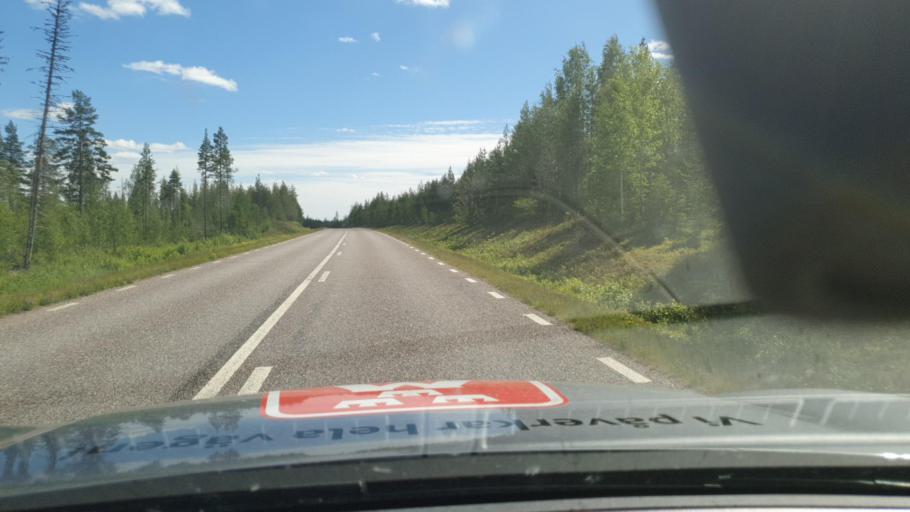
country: FI
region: Lapland
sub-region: Tunturi-Lappi
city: Kolari
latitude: 67.0441
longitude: 23.6868
